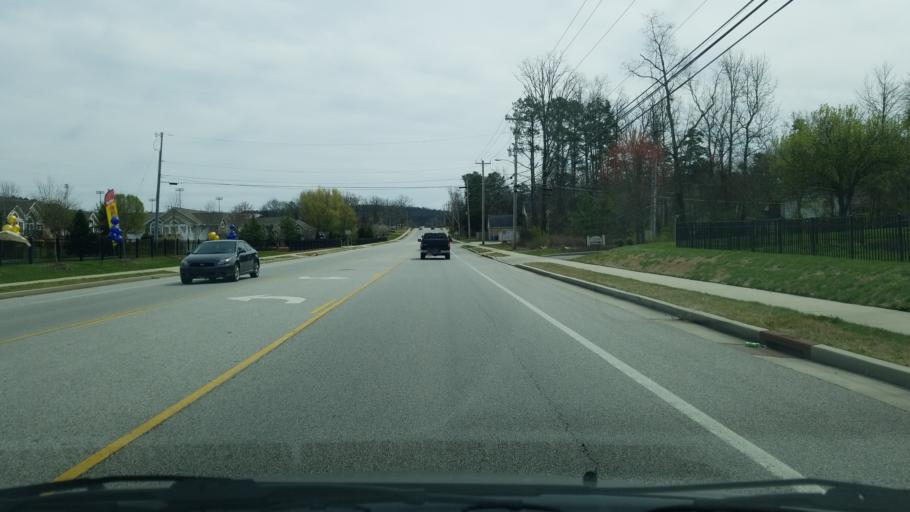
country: US
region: Tennessee
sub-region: Hamilton County
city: East Brainerd
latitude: 35.0367
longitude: -85.1402
